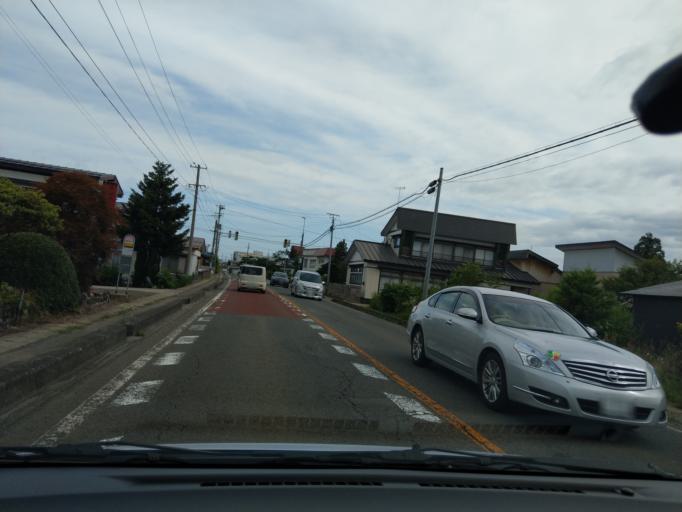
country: JP
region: Akita
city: Yokotemachi
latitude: 39.3992
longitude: 140.5635
